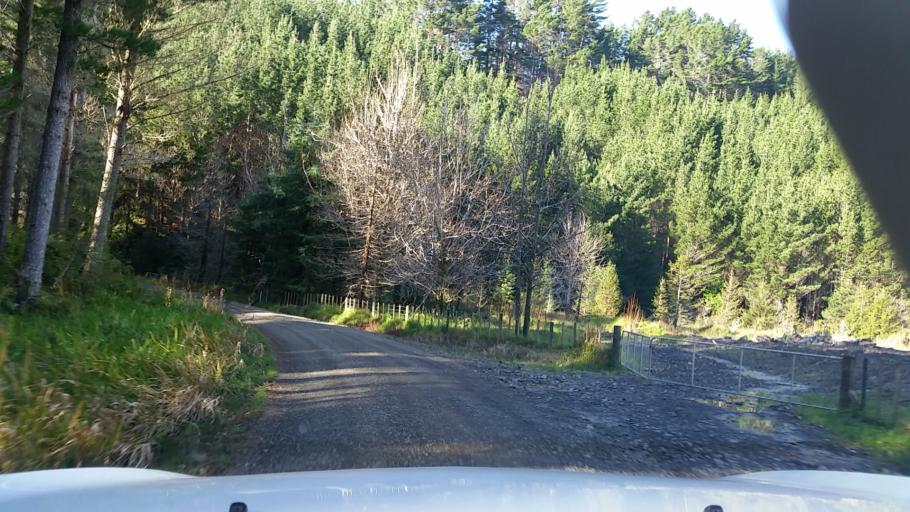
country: NZ
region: Taranaki
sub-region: New Plymouth District
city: Waitara
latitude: -38.9371
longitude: 174.5568
